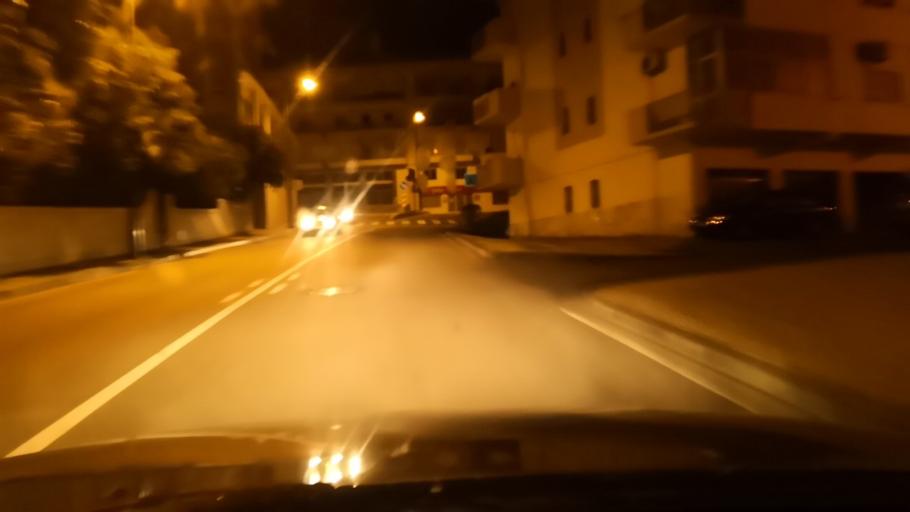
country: PT
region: Castelo Branco
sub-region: Concelho do Fundao
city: Fundao
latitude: 40.1363
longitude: -7.5050
